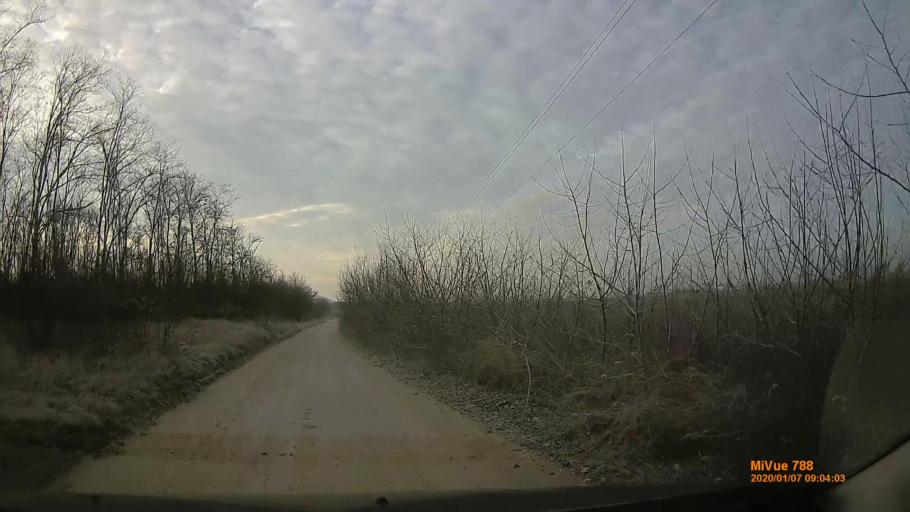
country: HU
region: Gyor-Moson-Sopron
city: Rajka
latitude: 47.9861
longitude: 17.1900
